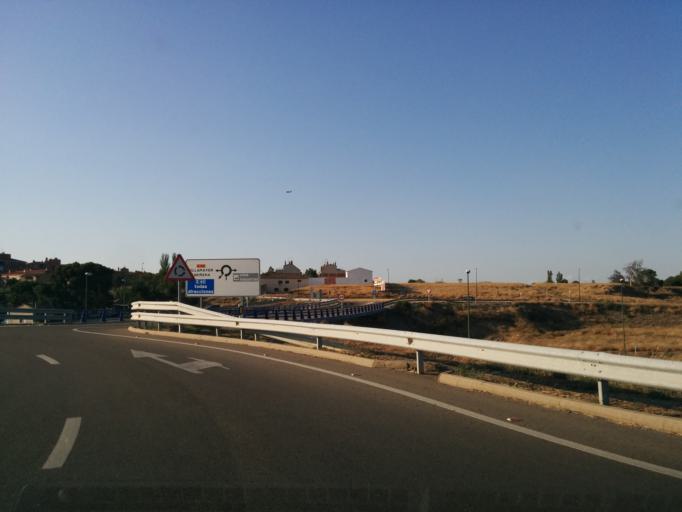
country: ES
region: Aragon
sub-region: Provincia de Zaragoza
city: Zaragoza
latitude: 41.6618
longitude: -0.8221
